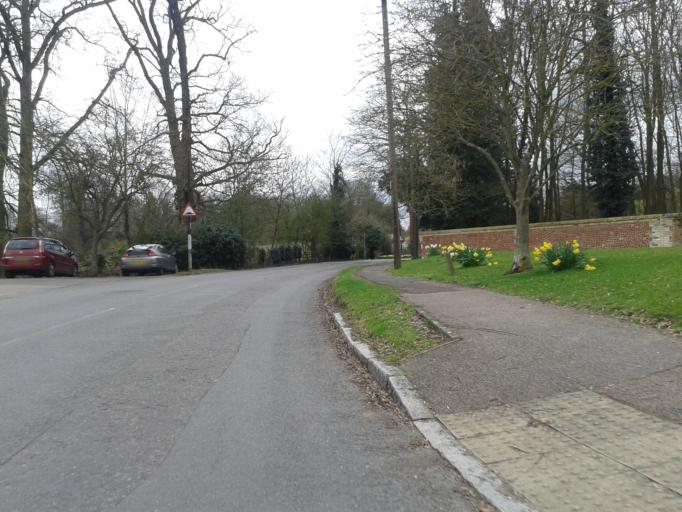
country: GB
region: England
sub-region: Cambridgeshire
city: Girton
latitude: 52.2254
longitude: 0.0429
